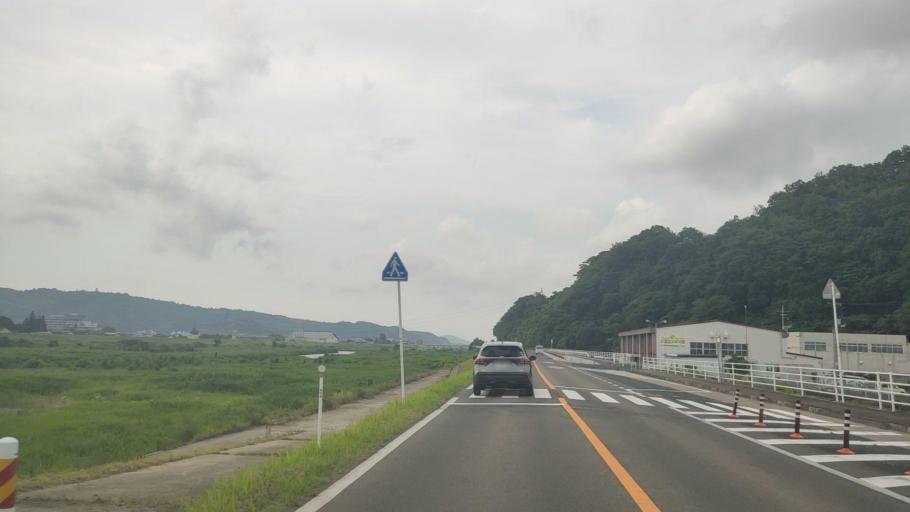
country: JP
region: Tottori
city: Kurayoshi
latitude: 35.4286
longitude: 133.8500
